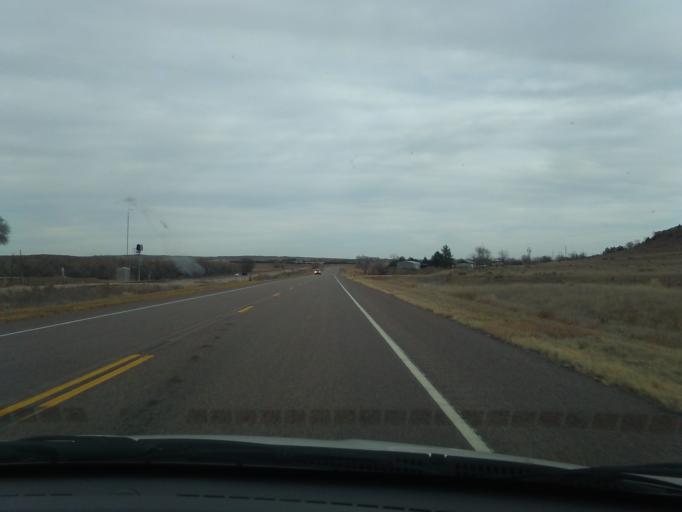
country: US
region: Colorado
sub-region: Yuma County
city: Wray
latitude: 40.0848
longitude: -102.1424
